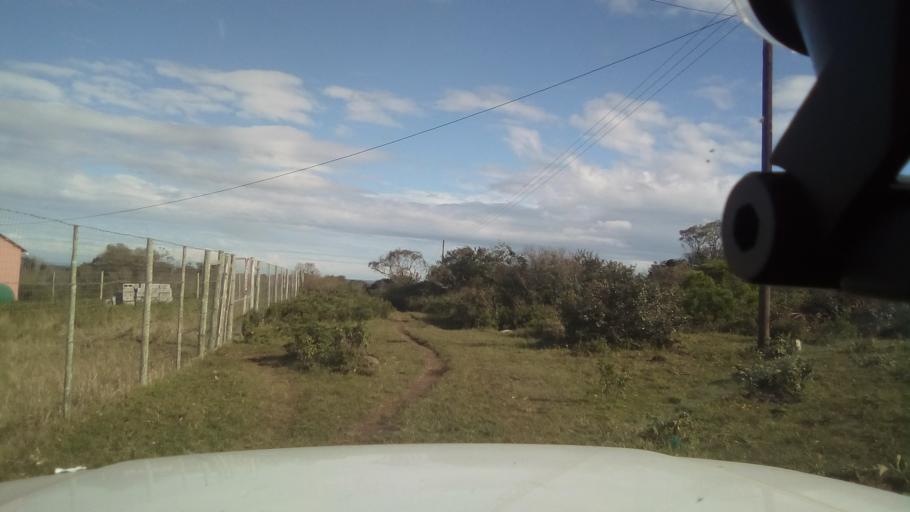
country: ZA
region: Eastern Cape
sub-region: Amathole District Municipality
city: Komga
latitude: -32.7751
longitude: 27.9326
